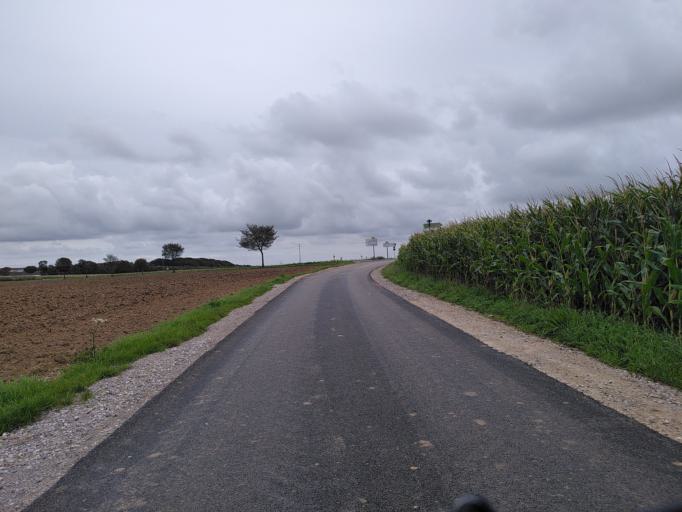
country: FR
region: Nord-Pas-de-Calais
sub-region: Departement du Pas-de-Calais
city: Desvres
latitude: 50.6441
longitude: 1.9655
